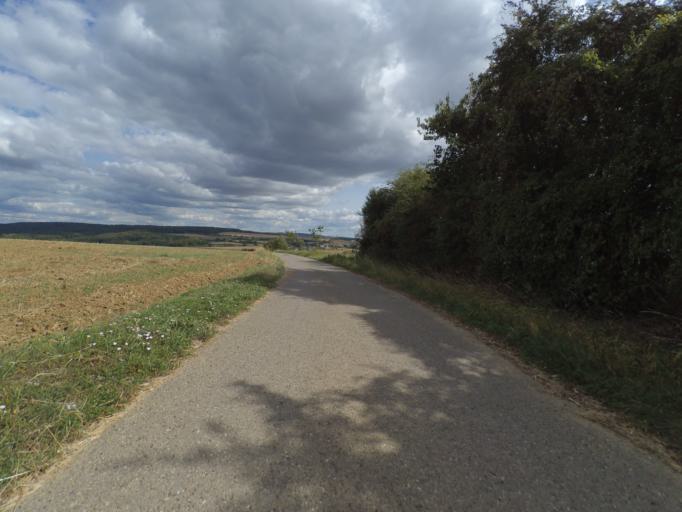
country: LU
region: Grevenmacher
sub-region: Canton de Remich
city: Mondorf-les-Bains
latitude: 49.5239
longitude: 6.2881
